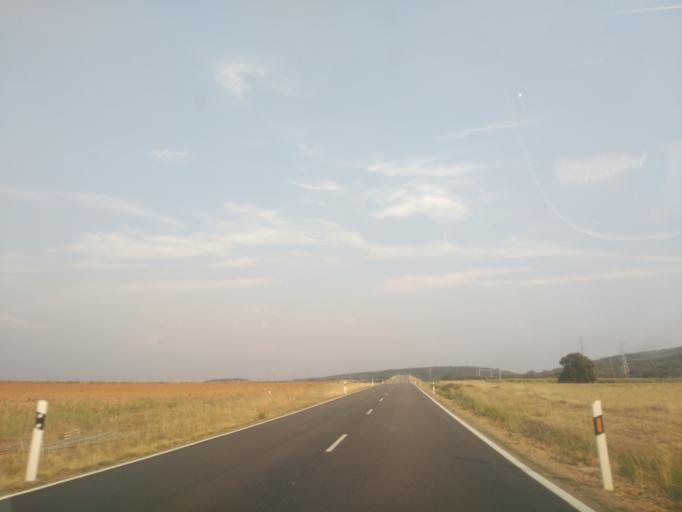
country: ES
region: Castille and Leon
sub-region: Provincia de Zamora
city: Moreruela de Tabara
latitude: 41.7652
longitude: -5.8668
